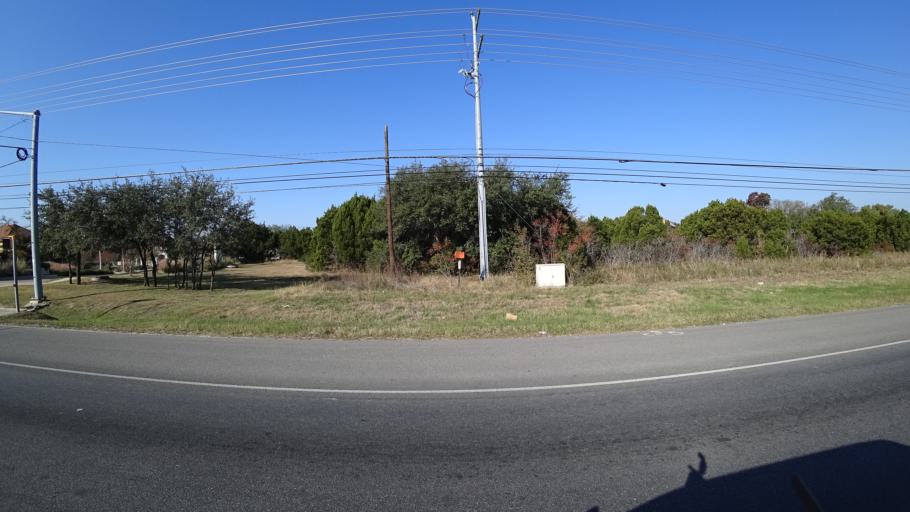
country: US
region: Texas
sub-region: Williamson County
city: Anderson Mill
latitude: 30.4292
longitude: -97.8426
